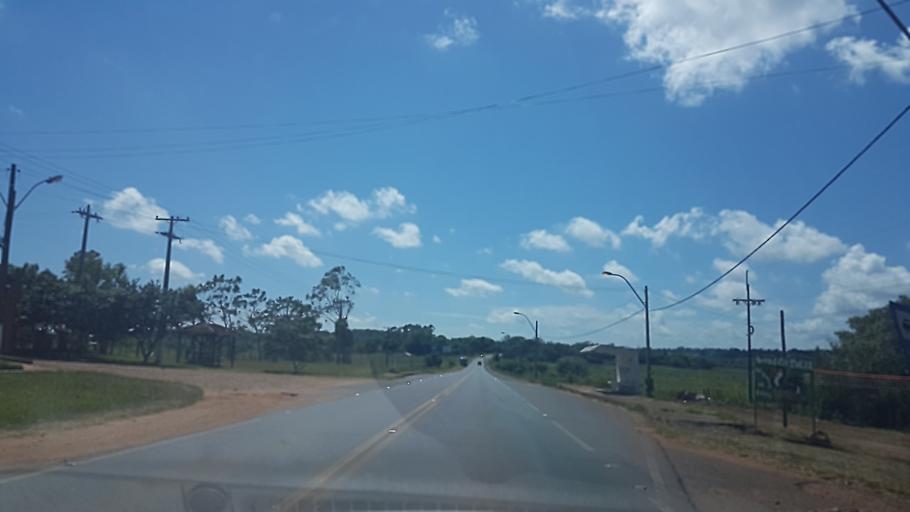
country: PY
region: Misiones
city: San Juan Bautista
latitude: -26.6740
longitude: -57.1126
